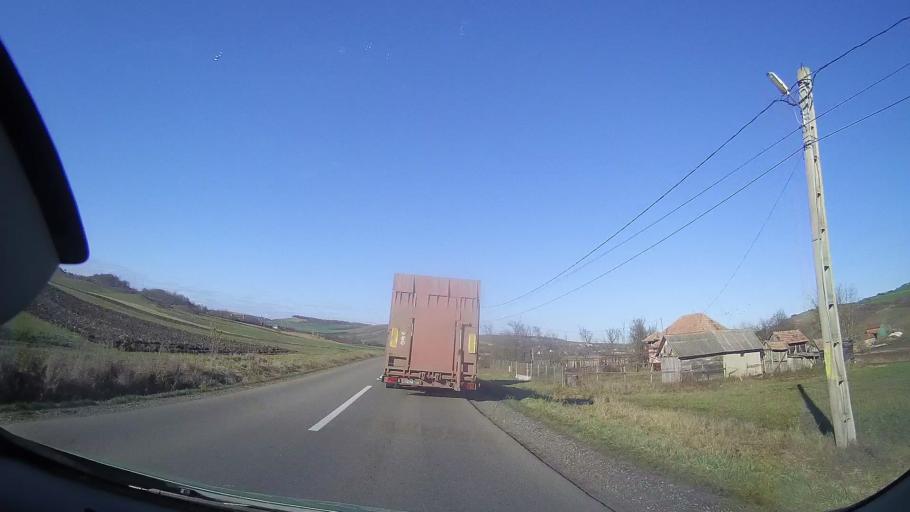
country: RO
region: Mures
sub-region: Comuna Sarmasu
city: Balda
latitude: 46.7171
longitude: 24.1480
